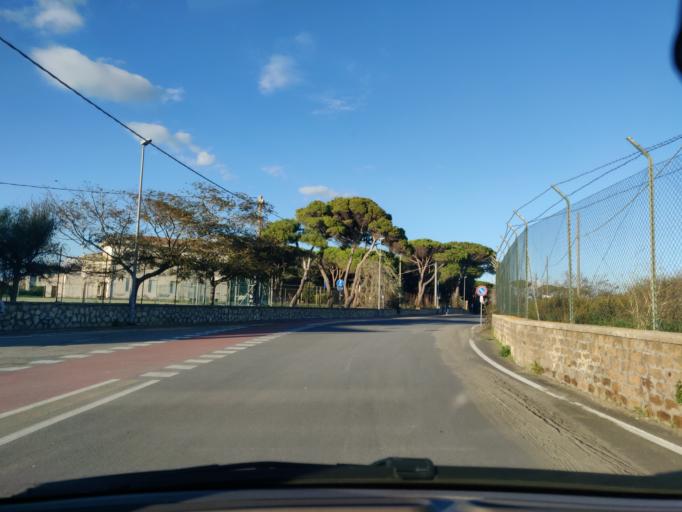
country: IT
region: Latium
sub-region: Provincia di Viterbo
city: Tarquinia
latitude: 42.2143
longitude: 11.7091
